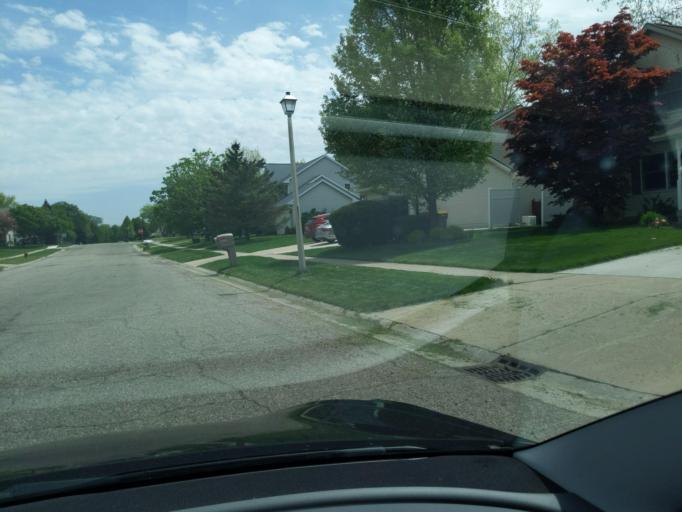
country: US
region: Michigan
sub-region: Ingham County
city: Holt
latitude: 42.6480
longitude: -84.5717
